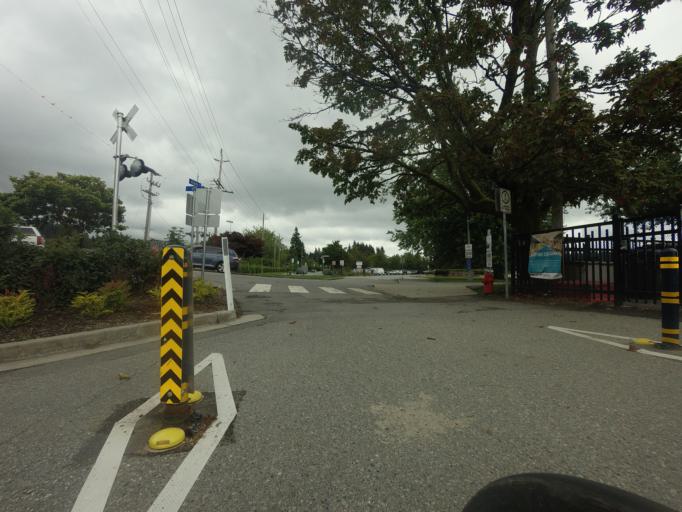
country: CA
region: British Columbia
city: West Vancouver
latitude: 49.3268
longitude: -123.1524
